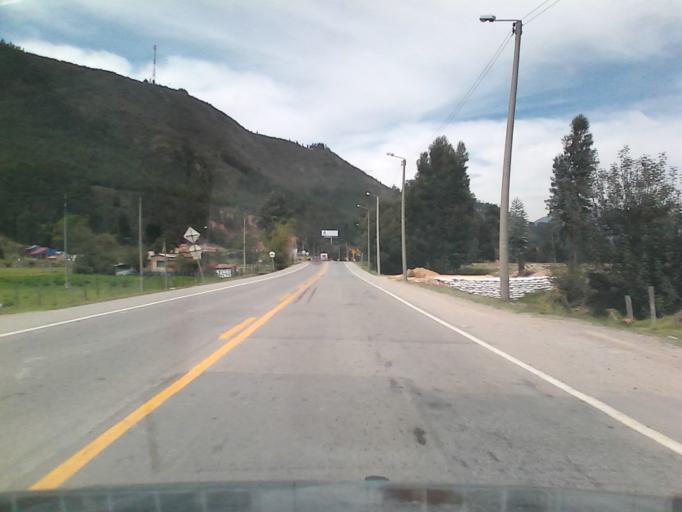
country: CO
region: Boyaca
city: Tibasosa
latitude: 5.7941
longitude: -72.9933
